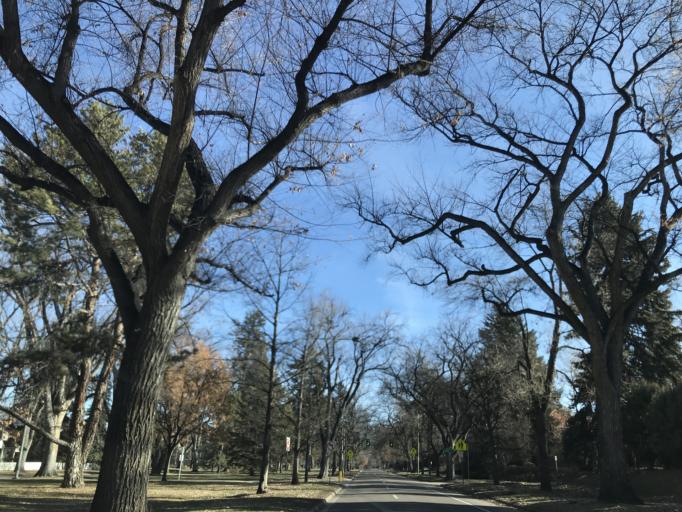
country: US
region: Colorado
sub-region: Arapahoe County
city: Glendale
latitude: 39.7254
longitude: -104.9390
